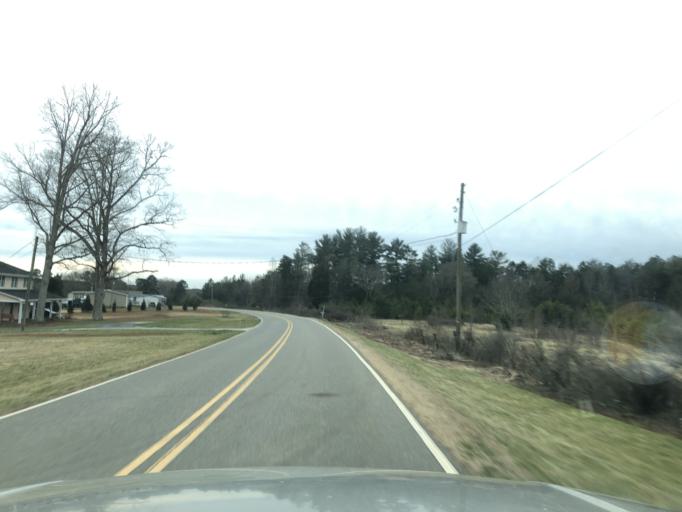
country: US
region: North Carolina
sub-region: Cleveland County
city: Shelby
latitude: 35.3404
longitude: -81.5329
